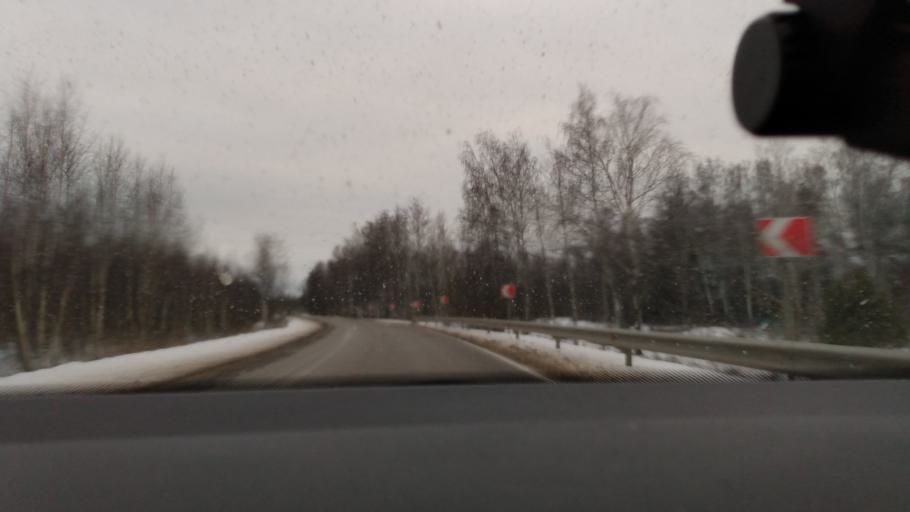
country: RU
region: Moskovskaya
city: Krasnaya Poyma
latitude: 55.1401
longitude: 39.2091
